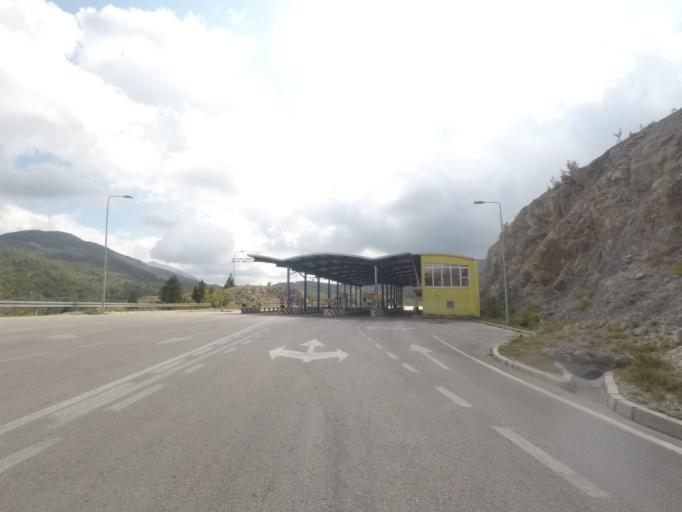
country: ME
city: Igalo
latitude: 42.5582
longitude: 18.4460
